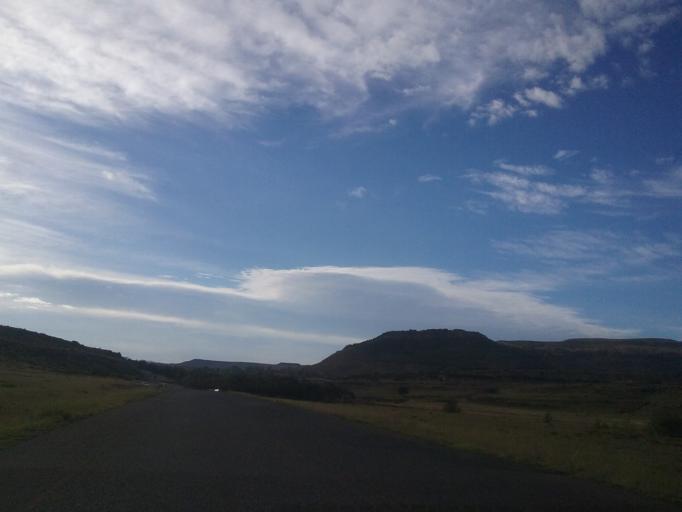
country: LS
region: Quthing
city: Quthing
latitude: -30.3870
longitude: 27.6031
